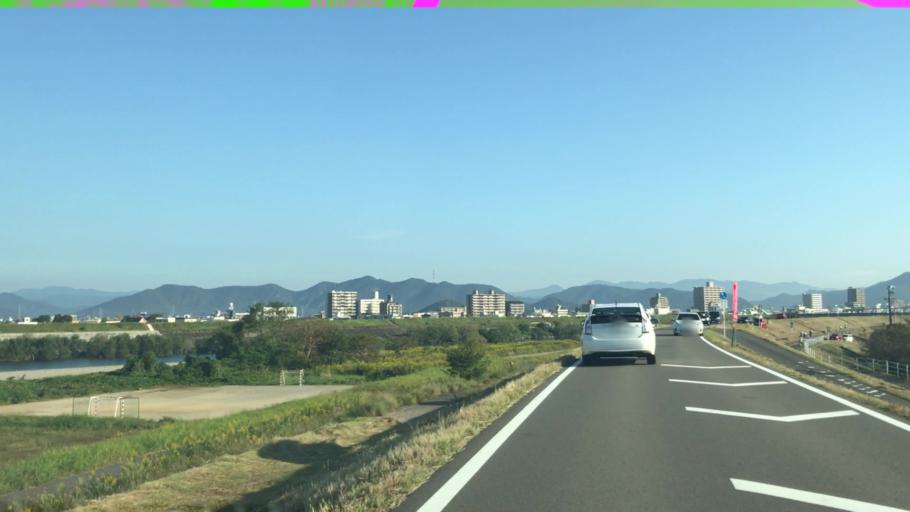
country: JP
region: Gifu
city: Gifu-shi
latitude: 35.4250
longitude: 136.7449
